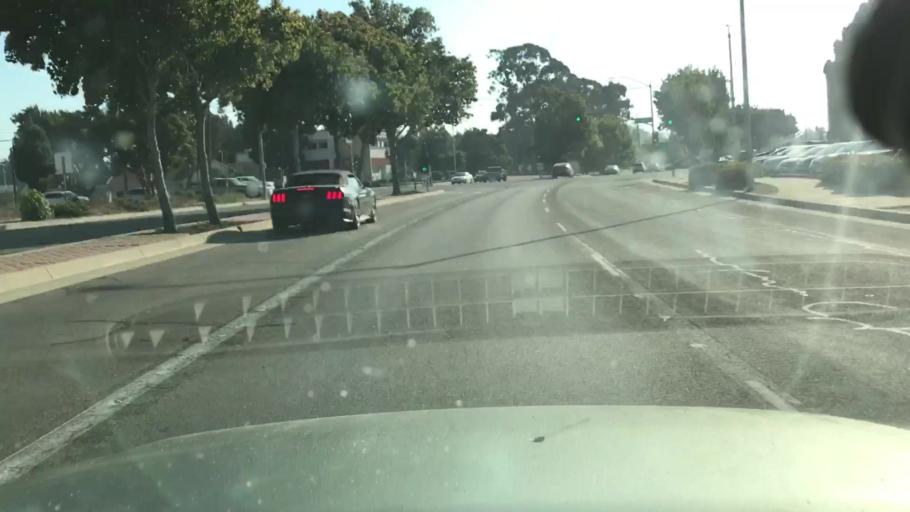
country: US
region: California
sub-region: Santa Barbara County
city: Santa Maria
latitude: 34.9100
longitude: -120.4334
